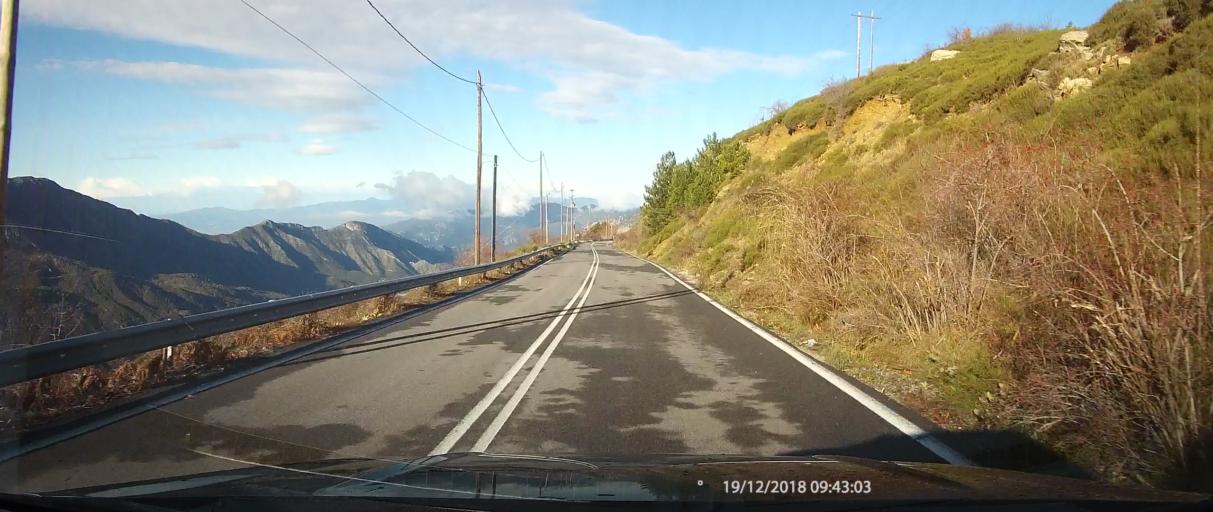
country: GR
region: Peloponnese
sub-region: Nomos Messinias
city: Paralia Vergas
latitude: 37.0701
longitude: 22.2602
